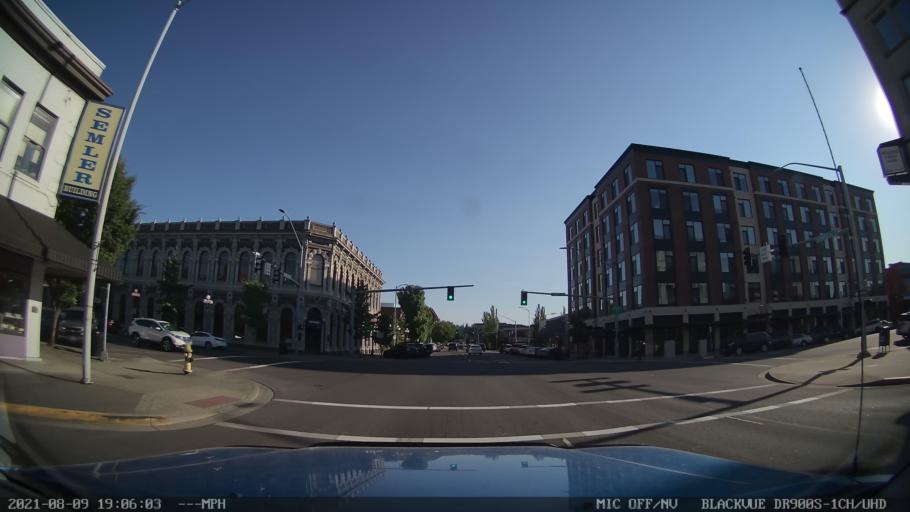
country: US
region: Oregon
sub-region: Marion County
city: Salem
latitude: 44.9406
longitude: -123.0404
